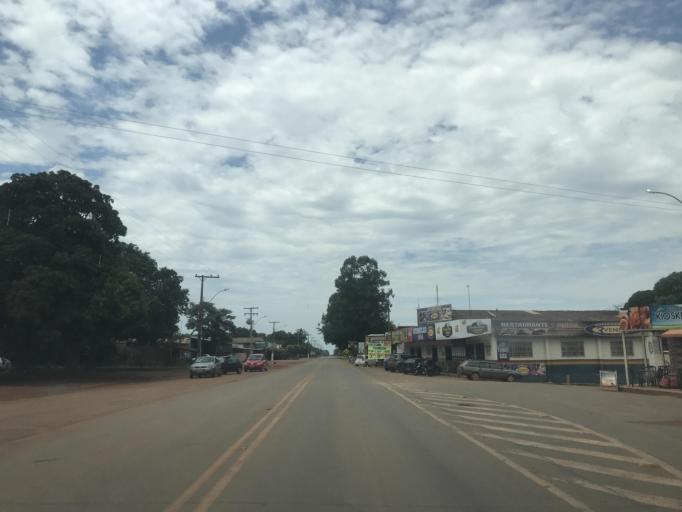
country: BR
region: Goias
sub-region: Luziania
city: Luziania
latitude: -16.3119
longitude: -48.0146
